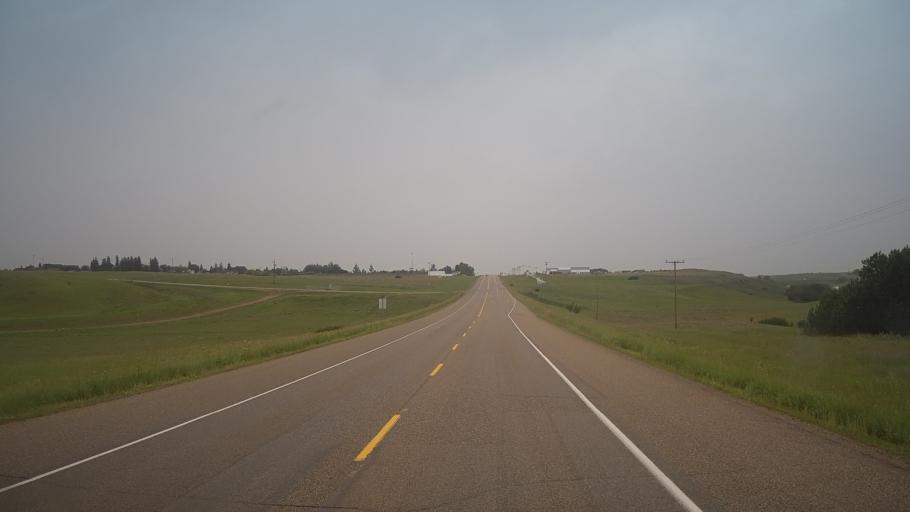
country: CA
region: Saskatchewan
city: Biggar
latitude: 52.0587
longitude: -107.9612
